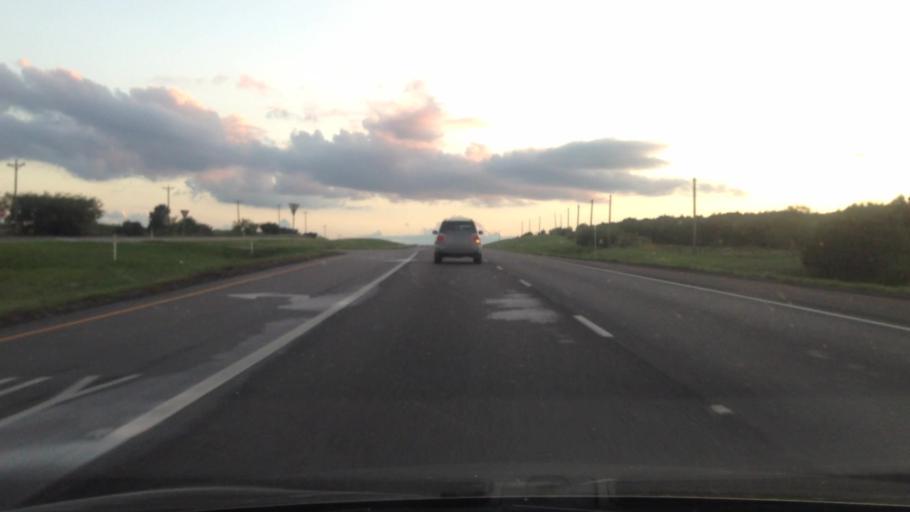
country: US
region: Texas
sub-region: Parker County
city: Aledo
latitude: 32.5961
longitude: -97.5792
